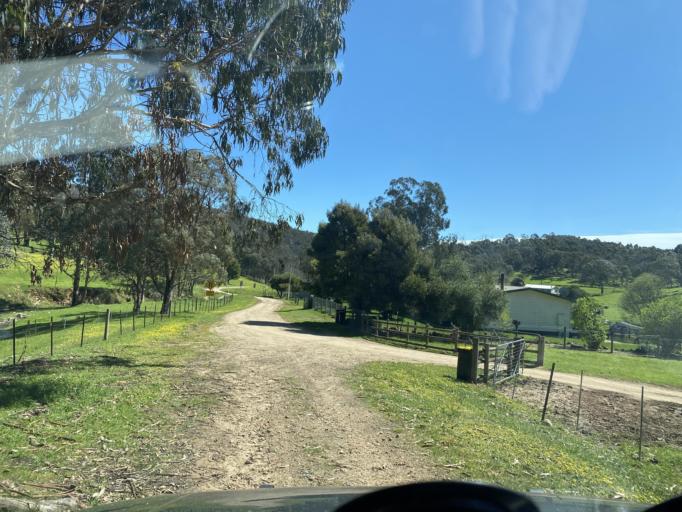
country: AU
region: Victoria
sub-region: Benalla
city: Benalla
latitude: -36.7122
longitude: 146.1818
